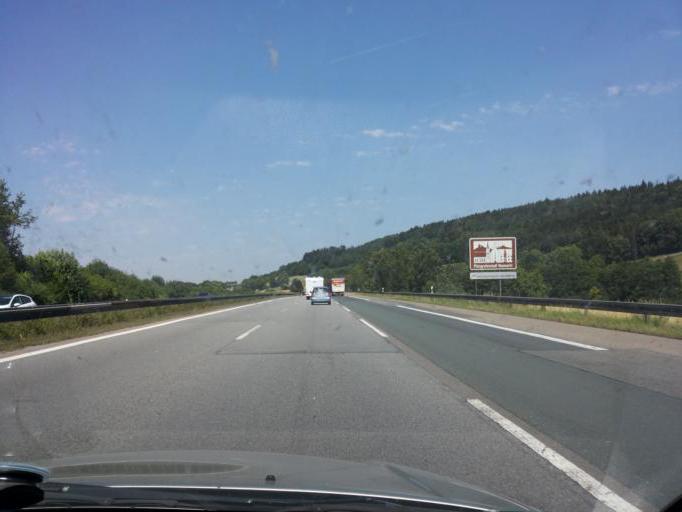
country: DE
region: Bavaria
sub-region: Regierungsbezirk Mittelfranken
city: Thalmassing
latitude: 49.1016
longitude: 11.2844
